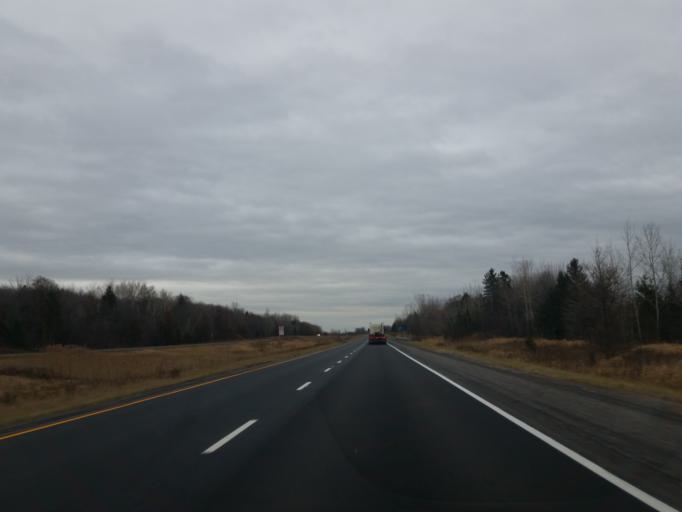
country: CA
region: Quebec
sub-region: Capitale-Nationale
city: Saint-Marc-des-Carrieres
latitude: 46.6033
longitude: -72.0935
